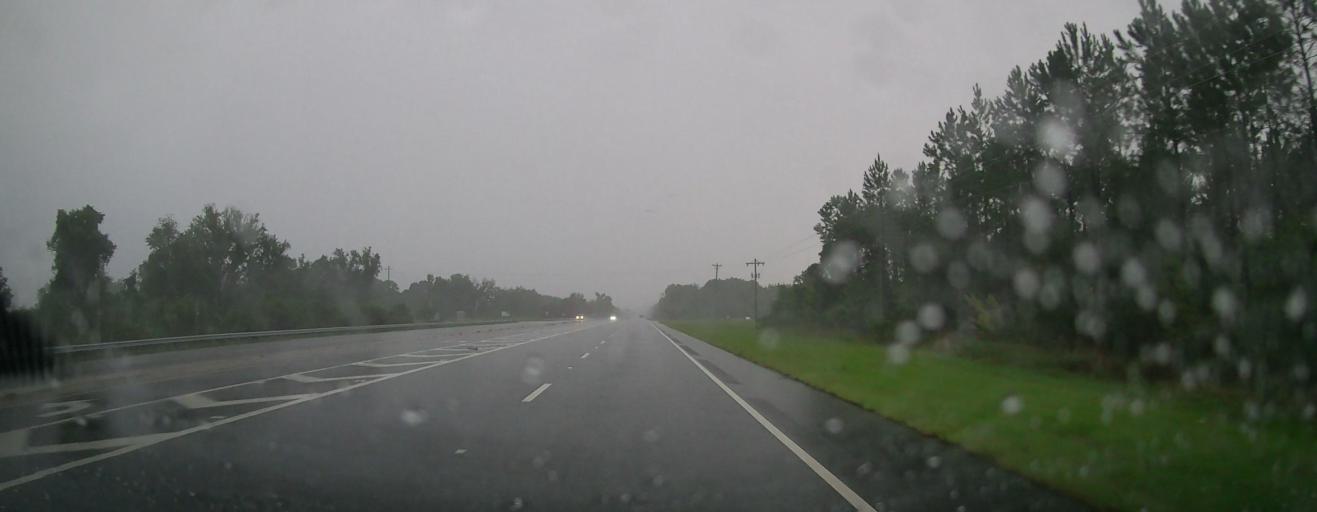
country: US
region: Georgia
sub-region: Clinch County
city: Homerville
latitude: 31.0520
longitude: -82.7061
